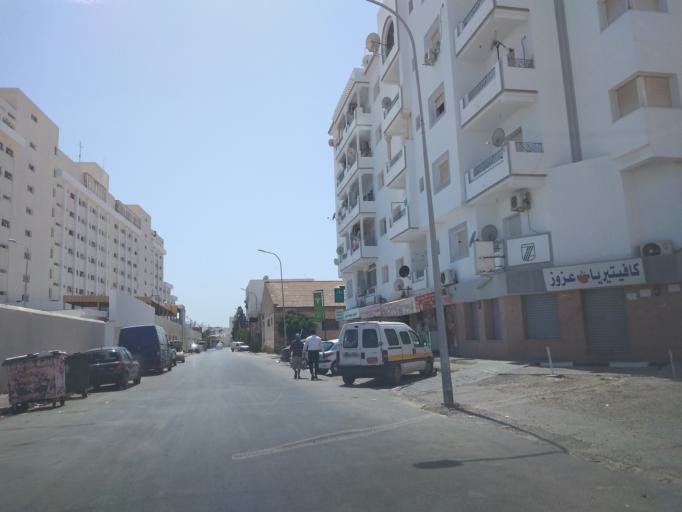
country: TN
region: Safaqis
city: Sfax
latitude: 34.7418
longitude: 10.7486
